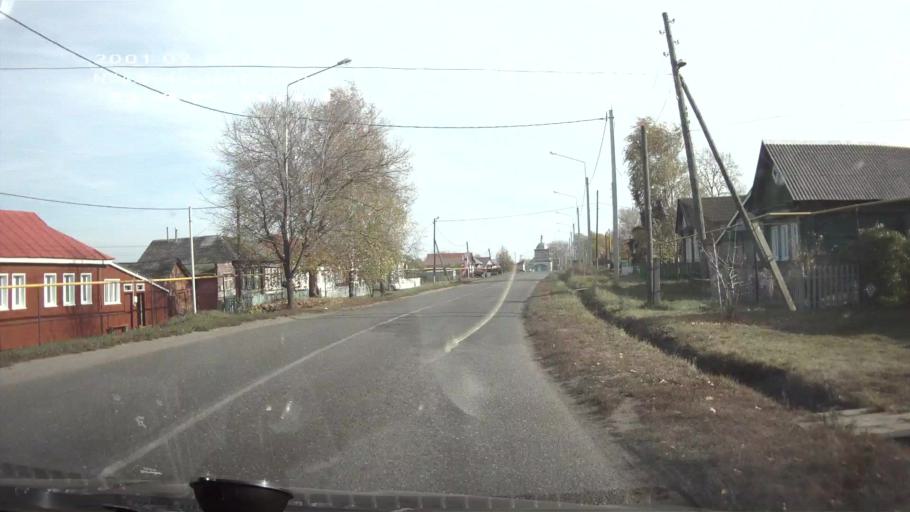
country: RU
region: Mordoviya
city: Turgenevo
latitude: 54.8547
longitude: 46.4039
